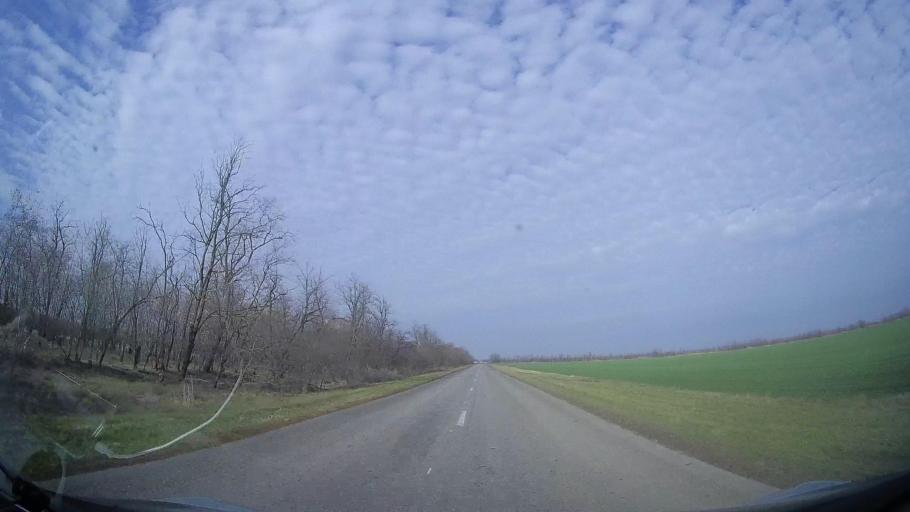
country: RU
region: Rostov
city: Gigant
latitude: 46.8724
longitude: 41.2739
